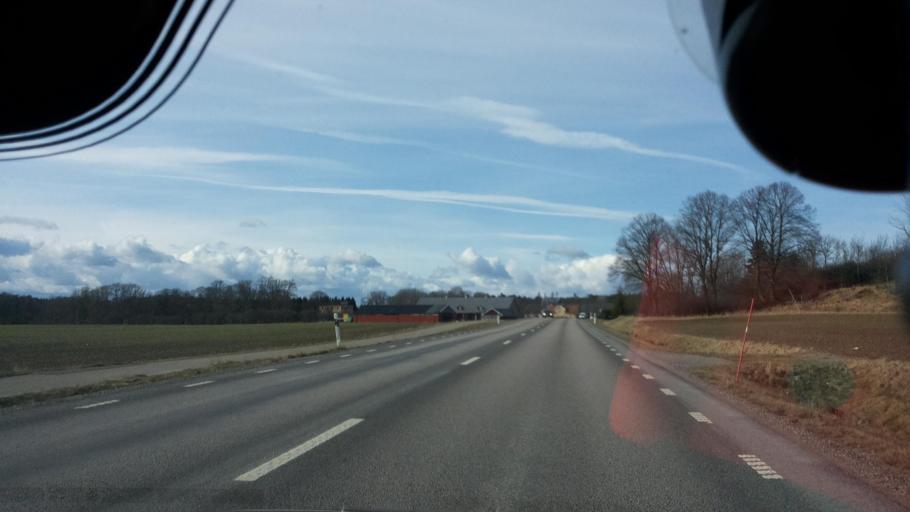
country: SE
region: Soedermanland
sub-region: Trosa Kommun
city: Trosa
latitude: 58.9240
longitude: 17.5383
